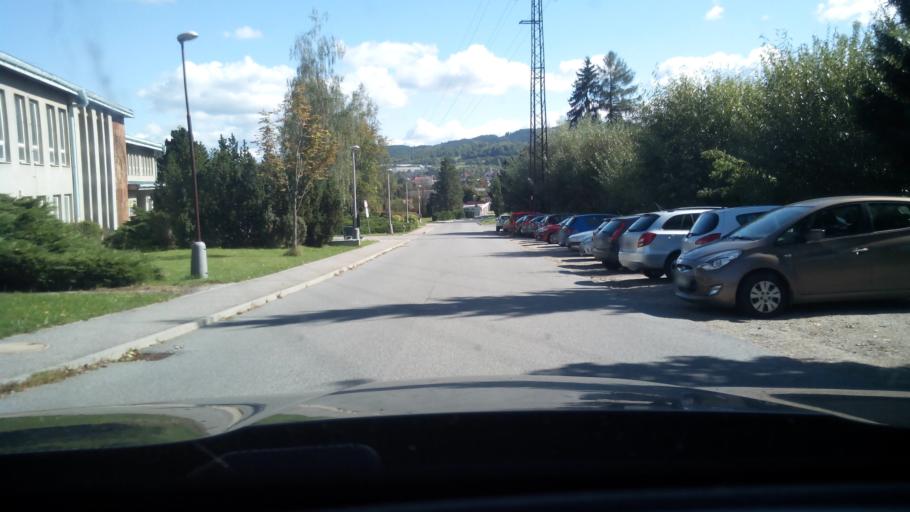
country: CZ
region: Jihocesky
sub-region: Okres Prachatice
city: Vimperk
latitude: 49.0591
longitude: 13.7748
